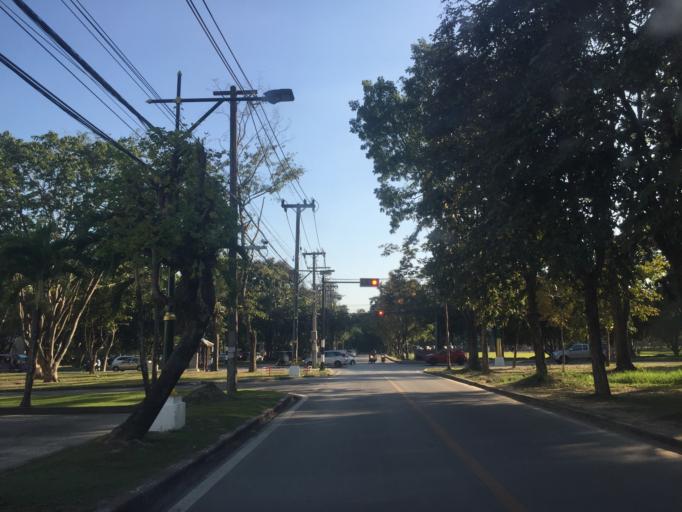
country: TH
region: Chiang Mai
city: Chiang Mai
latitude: 18.7965
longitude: 98.9573
